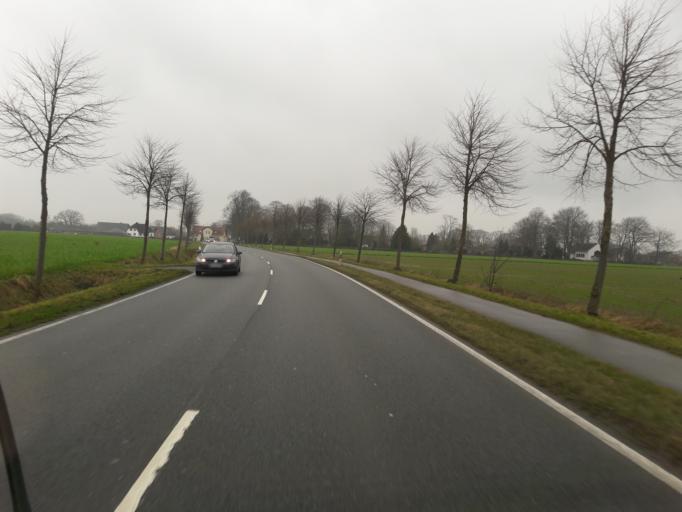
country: DE
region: North Rhine-Westphalia
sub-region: Regierungsbezirk Detmold
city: Hille
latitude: 52.3119
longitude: 8.8305
